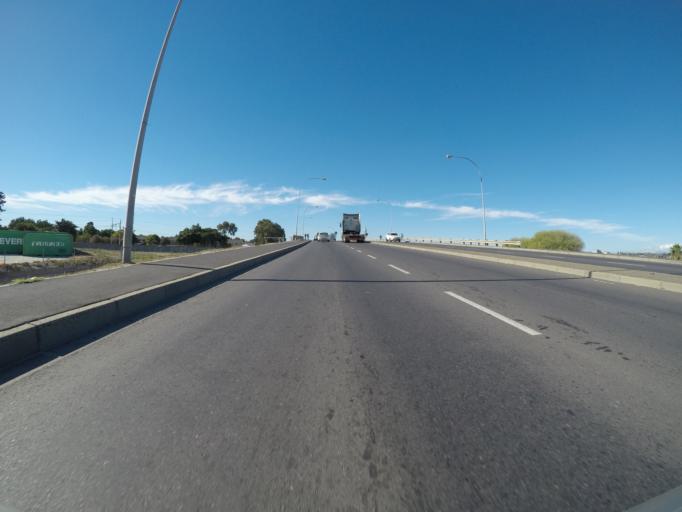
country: ZA
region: Western Cape
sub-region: City of Cape Town
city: Kraaifontein
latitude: -33.8944
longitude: 18.6724
